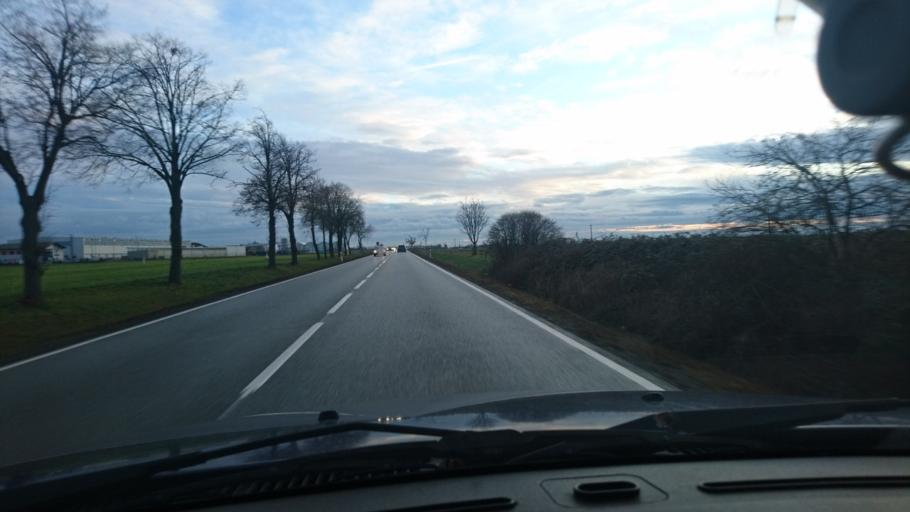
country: PL
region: Opole Voivodeship
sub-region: Powiat kluczborski
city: Kluczbork
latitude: 51.0060
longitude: 18.2047
